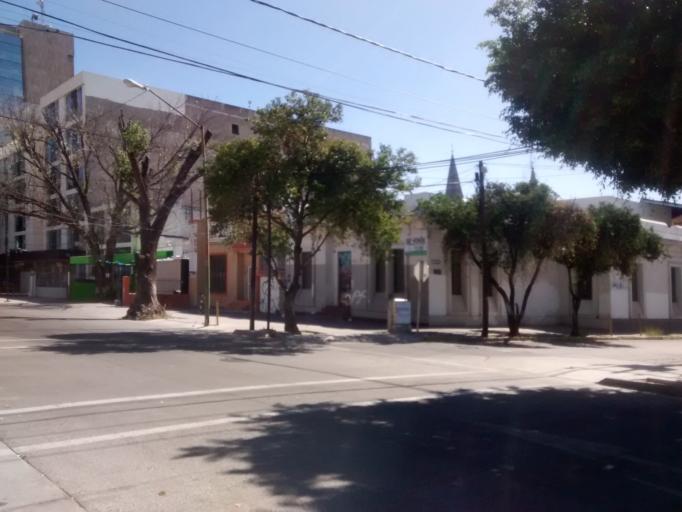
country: MX
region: Jalisco
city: Guadalajara
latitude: 20.6757
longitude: -103.3605
